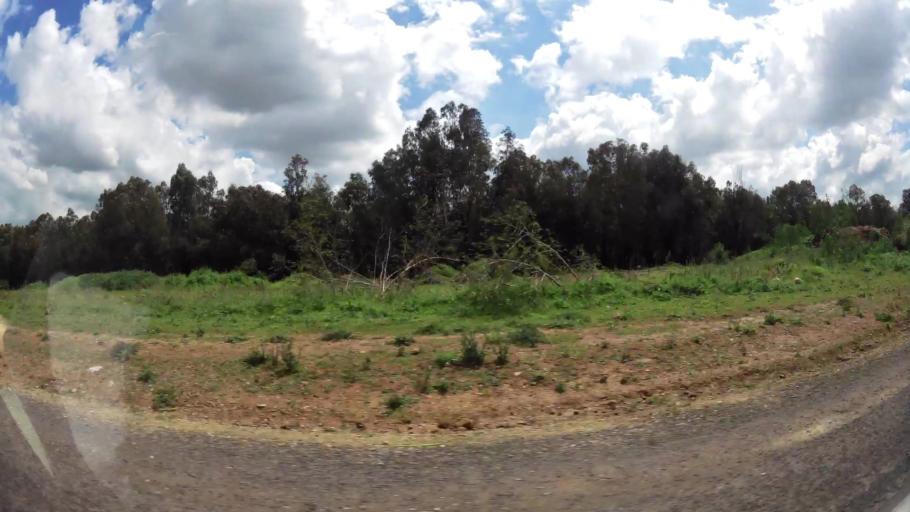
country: MA
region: Grand Casablanca
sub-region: Mediouna
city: Mediouna
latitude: 33.4040
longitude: -7.5593
